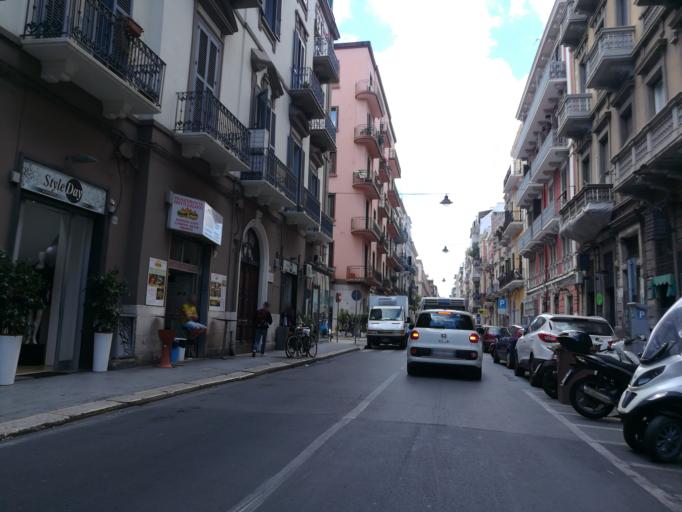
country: IT
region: Apulia
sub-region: Provincia di Bari
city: Bari
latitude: 41.1204
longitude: 16.8776
